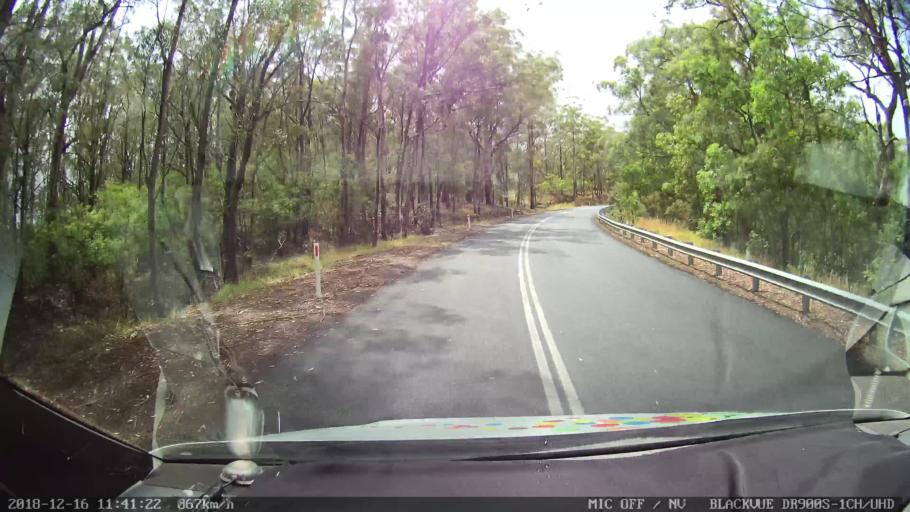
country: AU
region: New South Wales
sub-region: Tenterfield Municipality
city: Carrolls Creek
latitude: -28.9580
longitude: 152.2081
